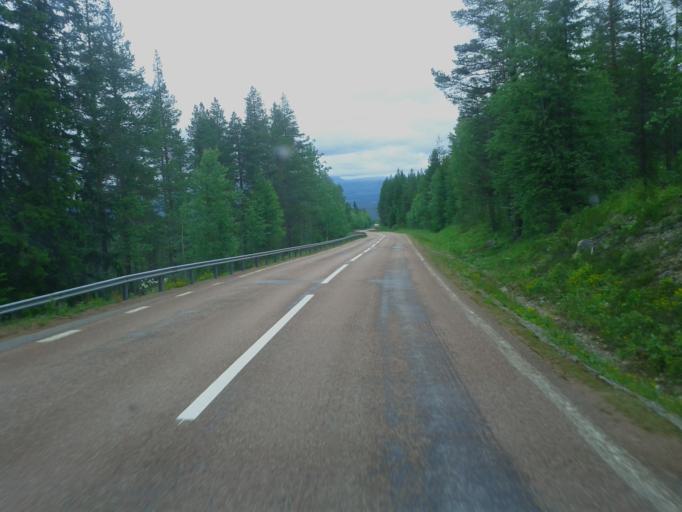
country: NO
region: Hedmark
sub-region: Trysil
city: Innbygda
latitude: 61.8460
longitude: 12.6006
